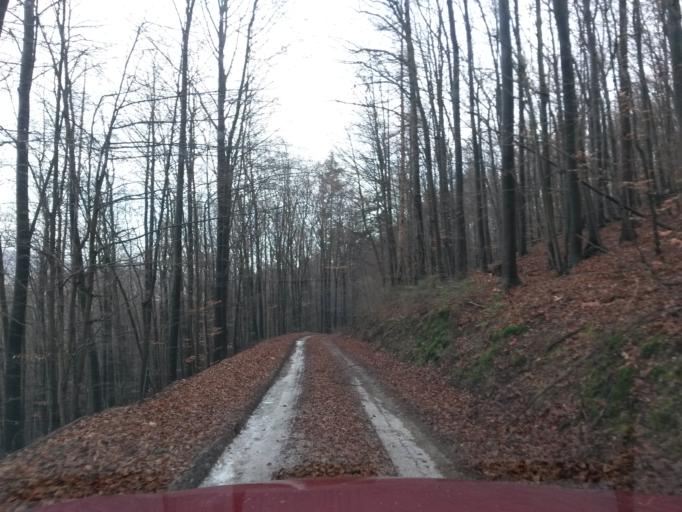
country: SK
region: Kosicky
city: Dobsina
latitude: 48.7495
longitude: 20.3961
